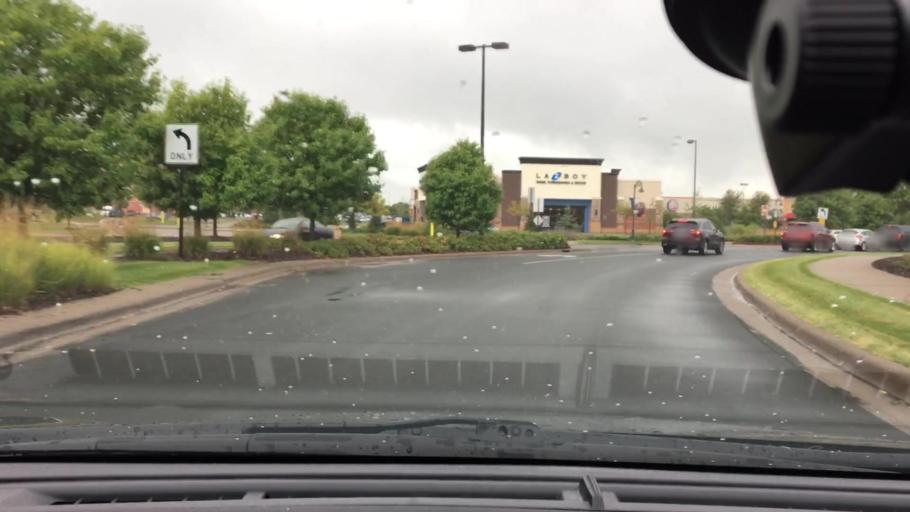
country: US
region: Minnesota
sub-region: Hennepin County
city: Maple Grove
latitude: 45.0919
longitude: -93.4260
